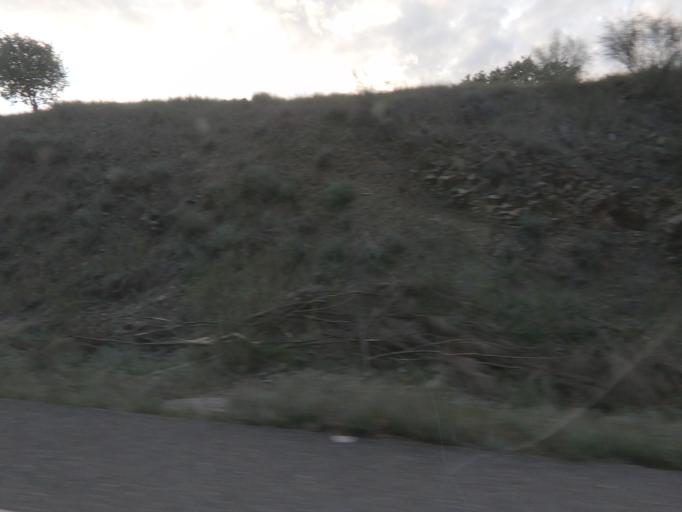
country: ES
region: Extremadura
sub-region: Provincia de Badajoz
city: La Roca de la Sierra
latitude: 39.1303
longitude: -6.6643
